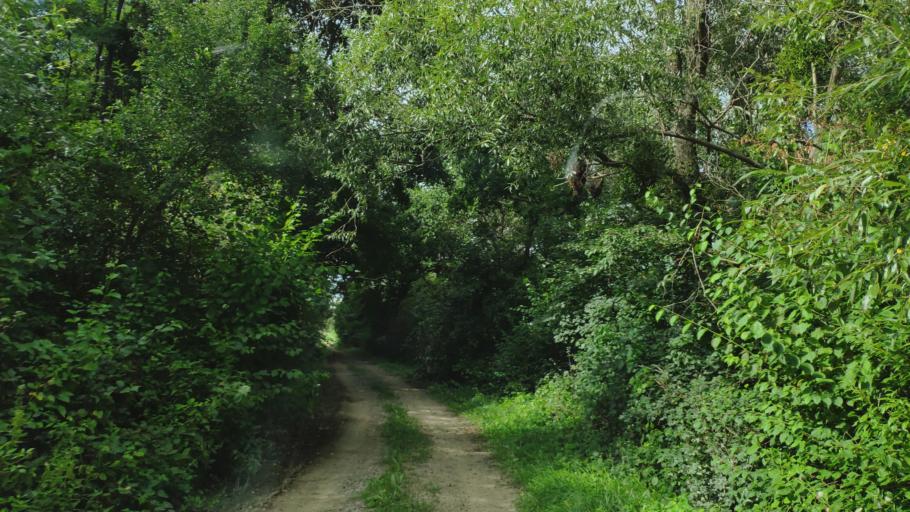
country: SK
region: Kosicky
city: Secovce
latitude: 48.6036
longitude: 21.5486
